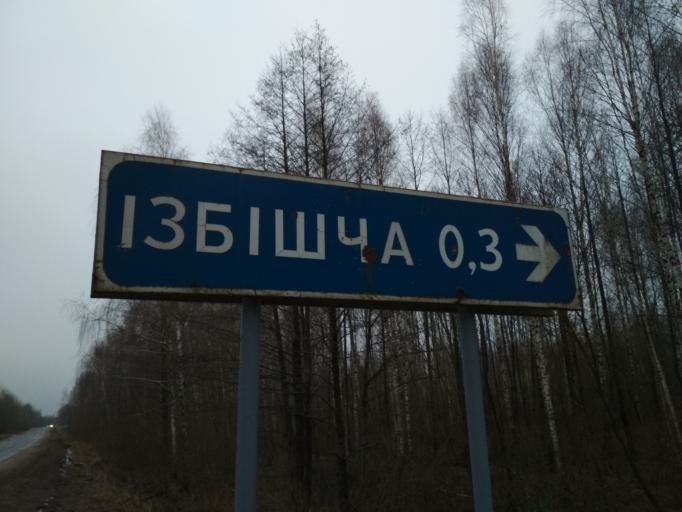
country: BY
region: Minsk
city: Mar''ina Horka
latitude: 53.4910
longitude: 28.1679
